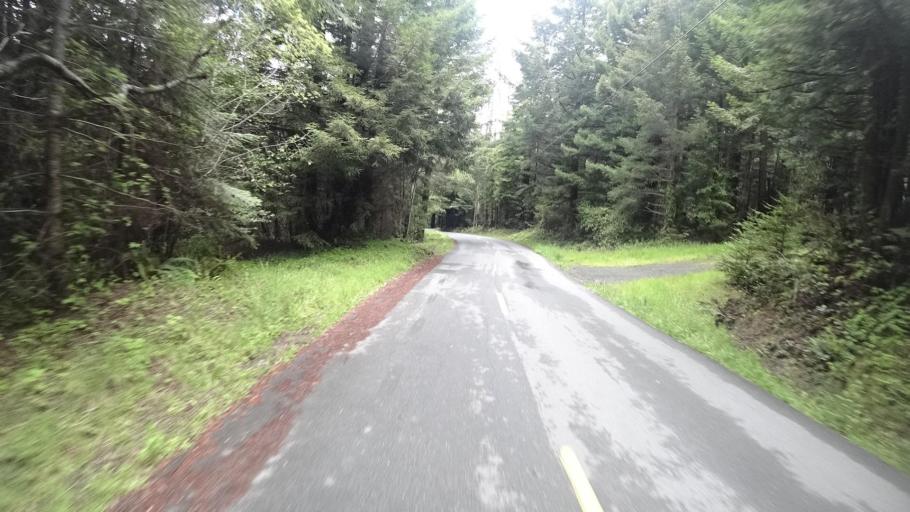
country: US
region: California
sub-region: Humboldt County
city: Blue Lake
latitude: 40.8697
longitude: -123.9543
